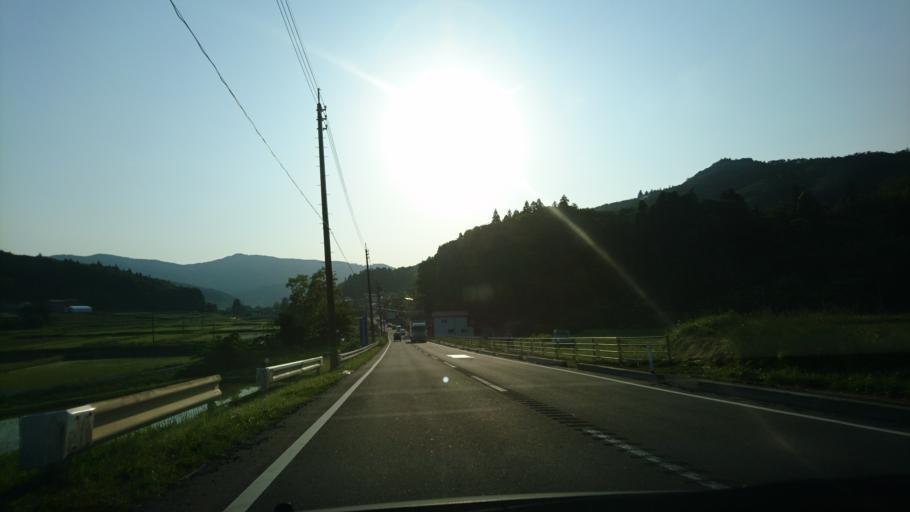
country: JP
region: Iwate
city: Ofunato
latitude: 38.9173
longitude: 141.4912
